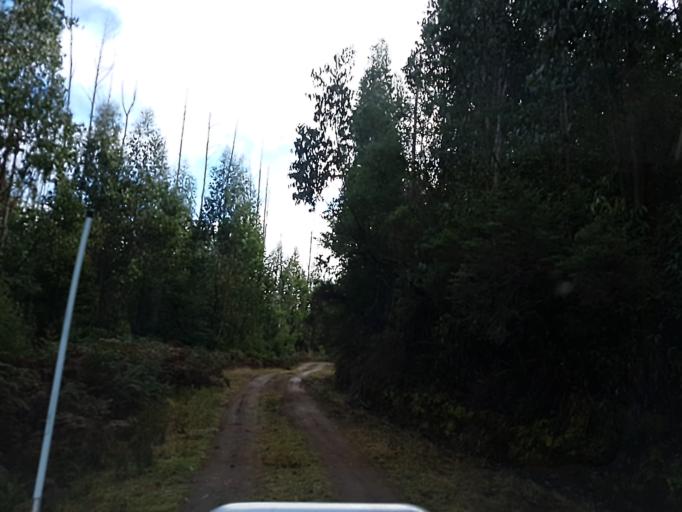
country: AU
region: Victoria
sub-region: Yarra Ranges
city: Millgrove
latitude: -37.5443
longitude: 145.7419
